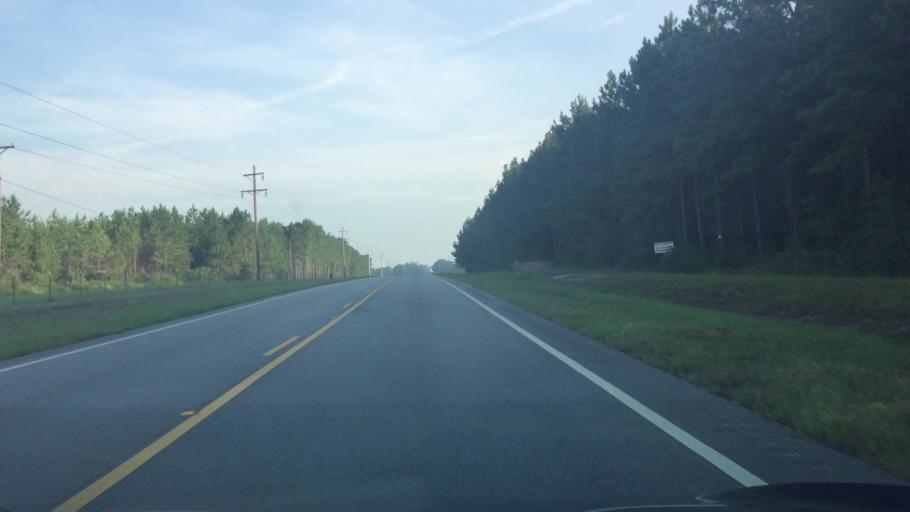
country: US
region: Alabama
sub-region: Covington County
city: Florala
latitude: 31.0404
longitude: -86.3799
